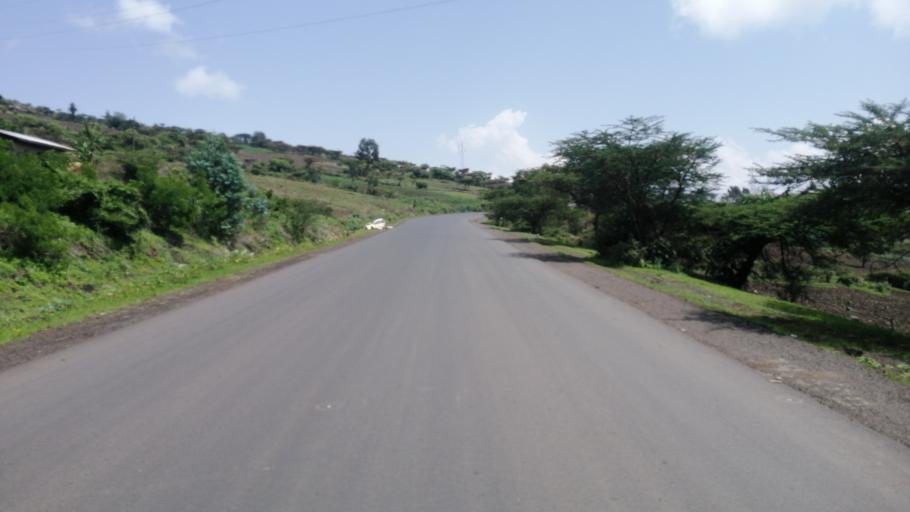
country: ET
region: Oromiya
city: Guder
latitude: 8.9892
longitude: 37.6260
